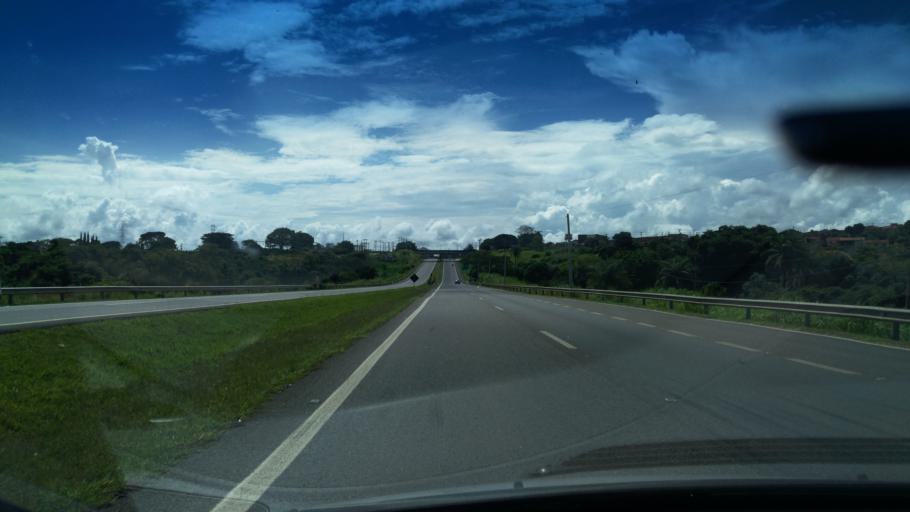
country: BR
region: Sao Paulo
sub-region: Santo Antonio Do Jardim
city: Espirito Santo do Pinhal
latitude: -22.1972
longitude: -46.7758
